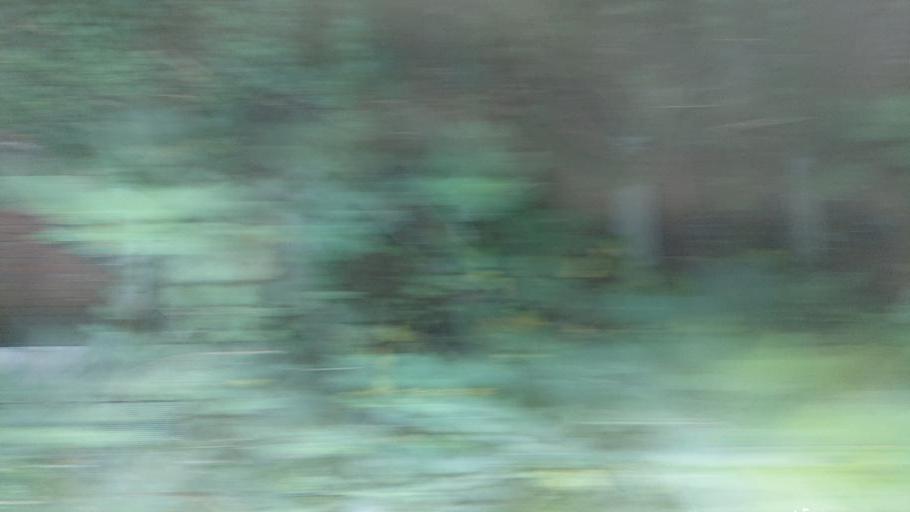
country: TW
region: Taiwan
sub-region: Hualien
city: Hualian
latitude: 23.9718
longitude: 121.5885
